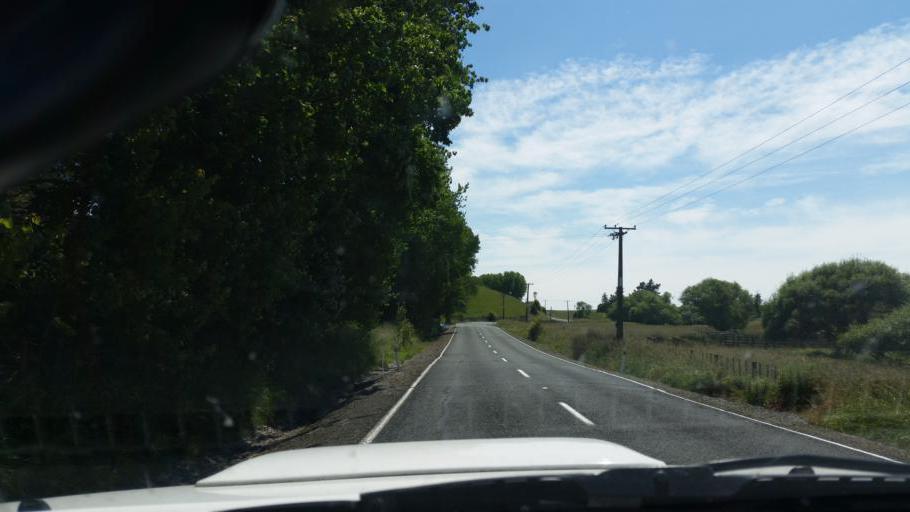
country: NZ
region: Auckland
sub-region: Auckland
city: Wellsford
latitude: -36.1915
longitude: 174.4034
